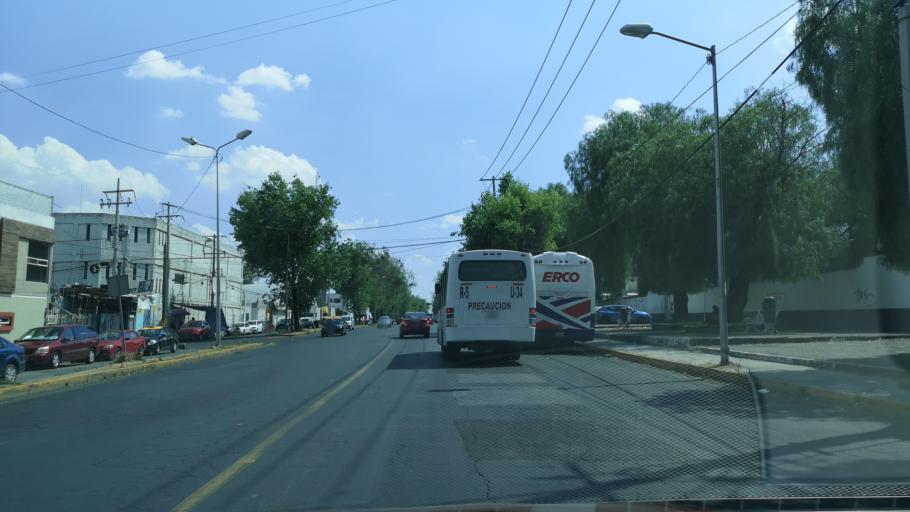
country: MX
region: Puebla
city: Puebla
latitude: 19.0778
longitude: -98.2172
